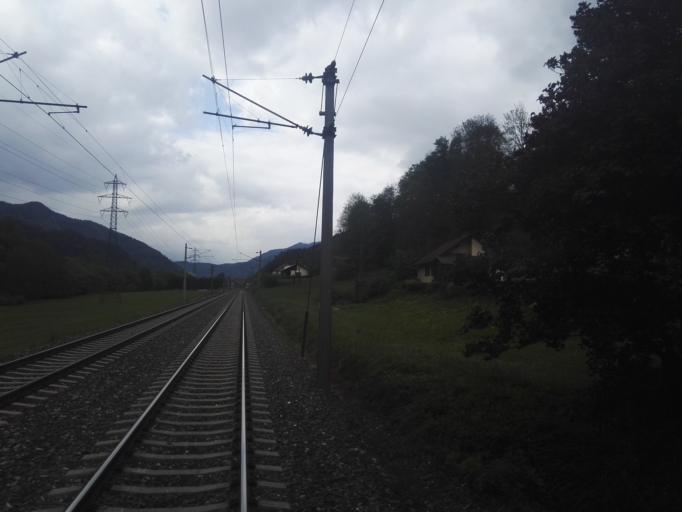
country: AT
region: Styria
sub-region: Politischer Bezirk Graz-Umgebung
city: Rothelstein
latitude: 47.3220
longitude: 15.3688
